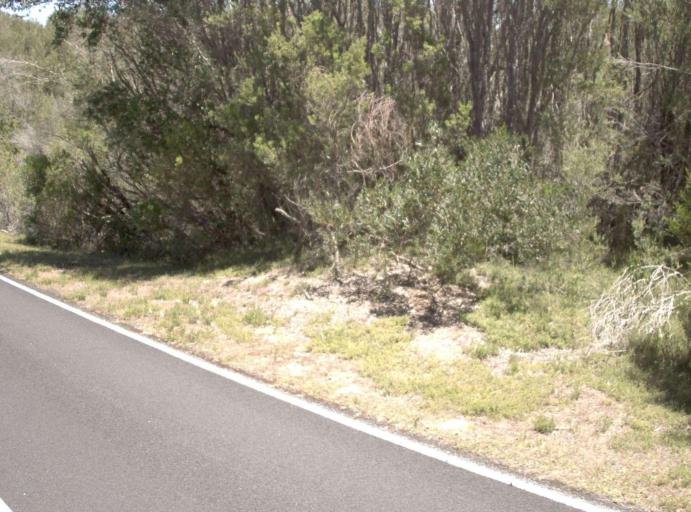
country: AU
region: Victoria
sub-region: Latrobe
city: Morwell
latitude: -38.8809
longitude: 146.2643
